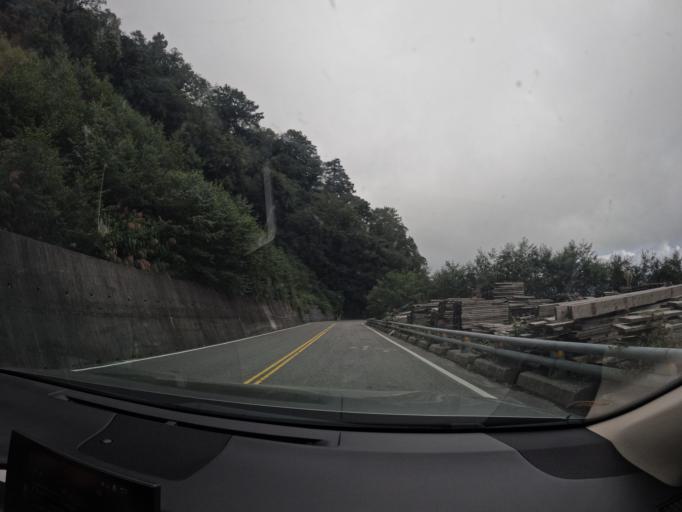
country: TW
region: Taiwan
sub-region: Taitung
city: Taitung
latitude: 23.2458
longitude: 120.9944
